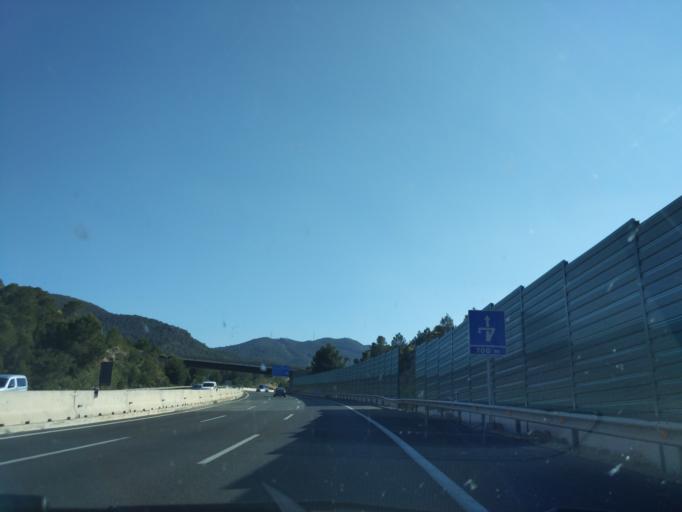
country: ES
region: Murcia
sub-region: Murcia
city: Murcia
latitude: 37.9264
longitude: -1.1570
